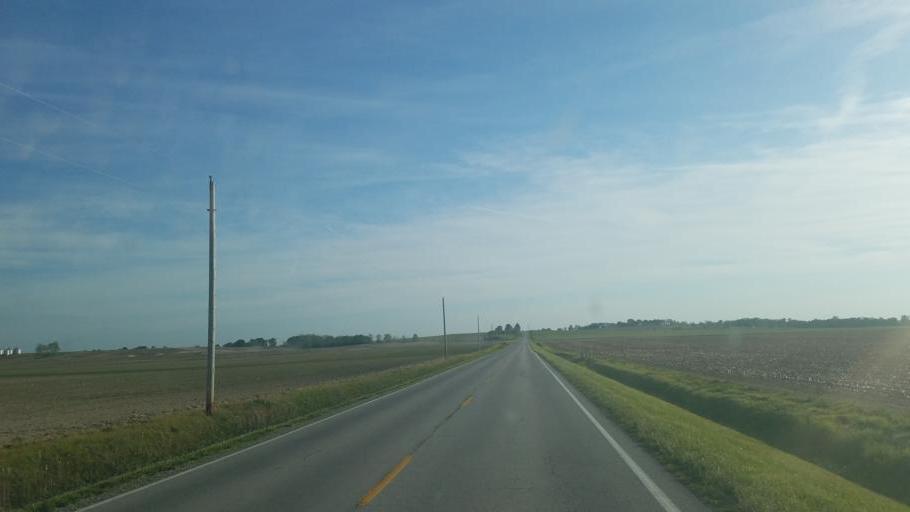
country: US
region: Ohio
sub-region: Highland County
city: Greenfield
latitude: 39.3798
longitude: -83.3423
